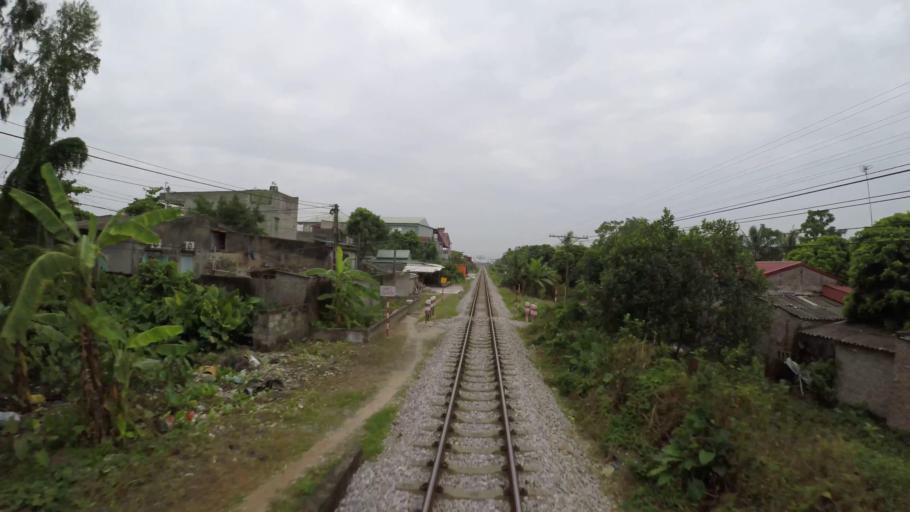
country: VN
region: Hai Duong
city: Nam Sach
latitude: 20.9776
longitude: 106.4105
